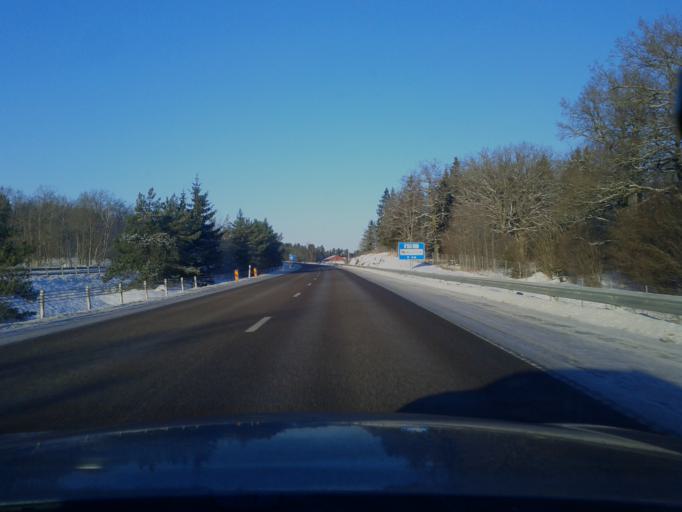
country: SE
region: Uppsala
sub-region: Knivsta Kommun
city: Knivsta
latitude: 59.7255
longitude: 17.8371
